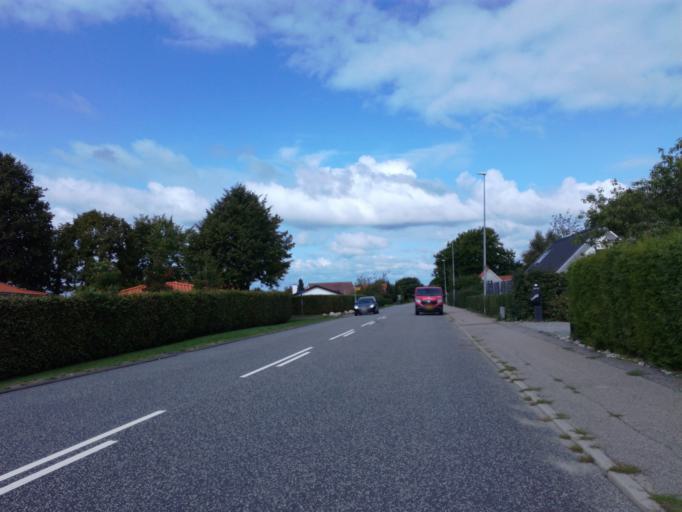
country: DK
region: South Denmark
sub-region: Vejle Kommune
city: Vejle
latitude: 55.6769
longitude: 9.5680
